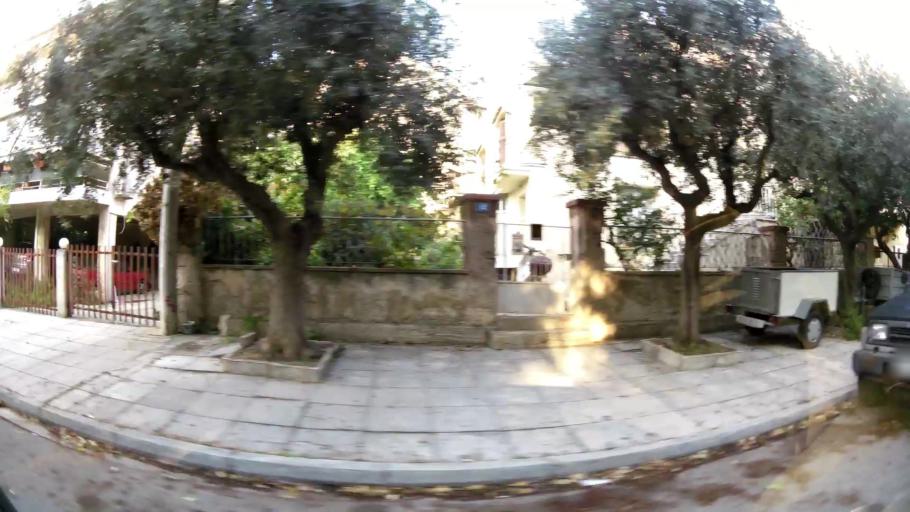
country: GR
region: Attica
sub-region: Nomarchia Athinas
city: Agios Dimitrios
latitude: 37.9366
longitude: 23.7461
